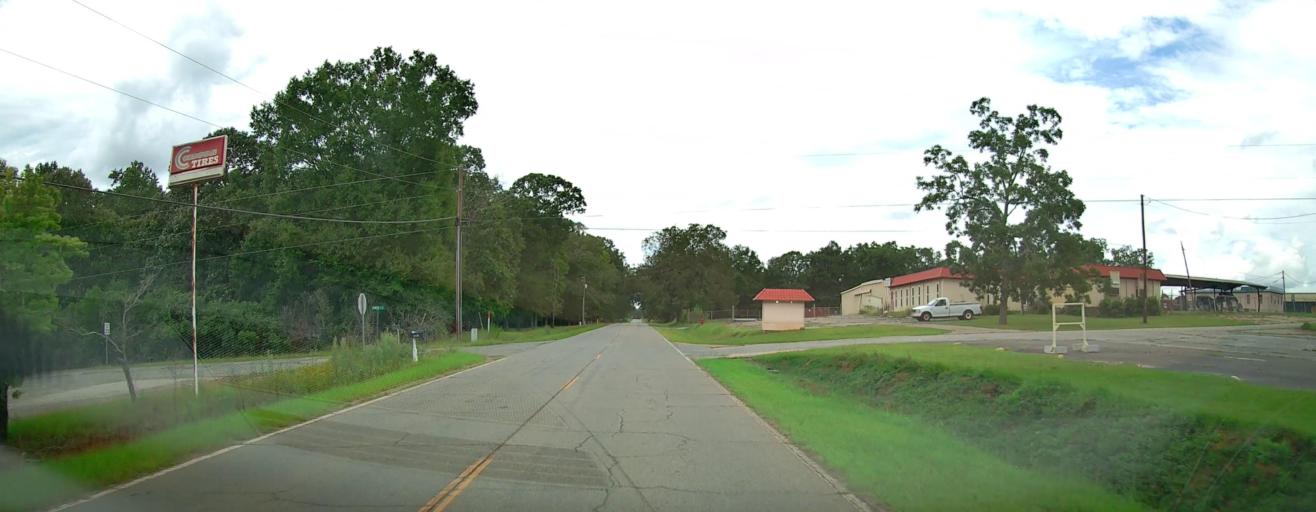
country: US
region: Georgia
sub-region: Schley County
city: Ellaville
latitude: 32.2213
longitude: -84.2964
